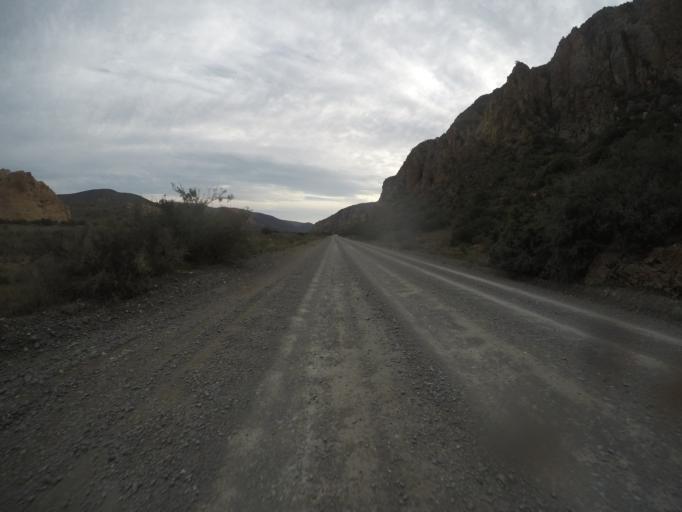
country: ZA
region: Eastern Cape
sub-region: Cacadu District Municipality
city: Willowmore
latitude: -33.5196
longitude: 23.6703
